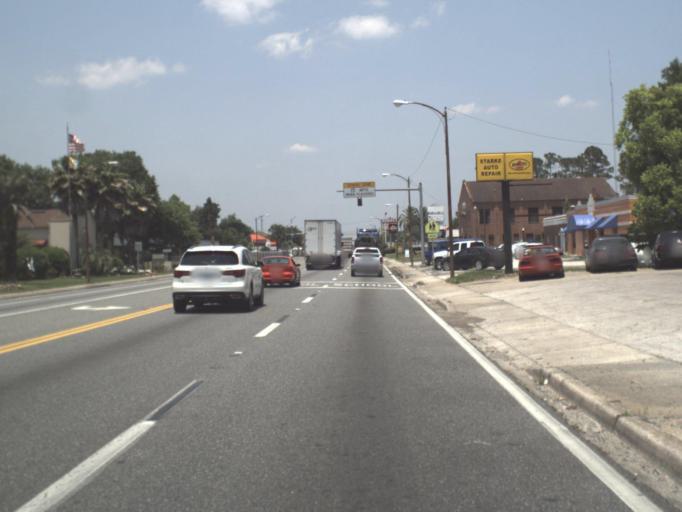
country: US
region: Florida
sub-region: Bradford County
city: Starke
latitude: 29.9477
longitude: -82.1103
